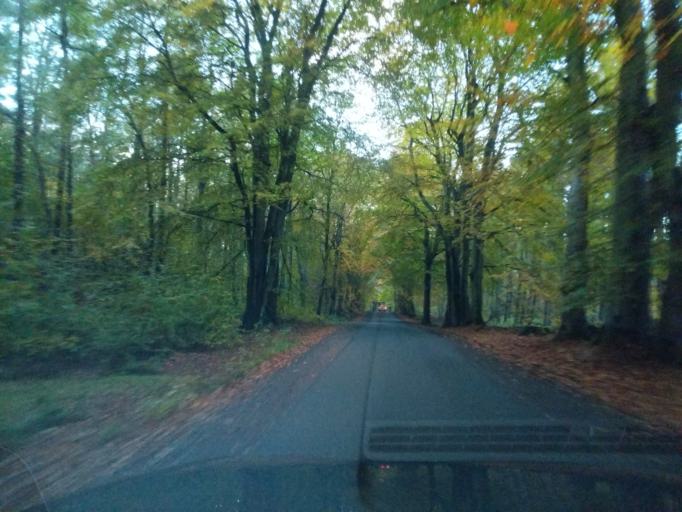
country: GB
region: Scotland
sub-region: Fife
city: Leuchars
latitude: 56.4038
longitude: -2.8372
